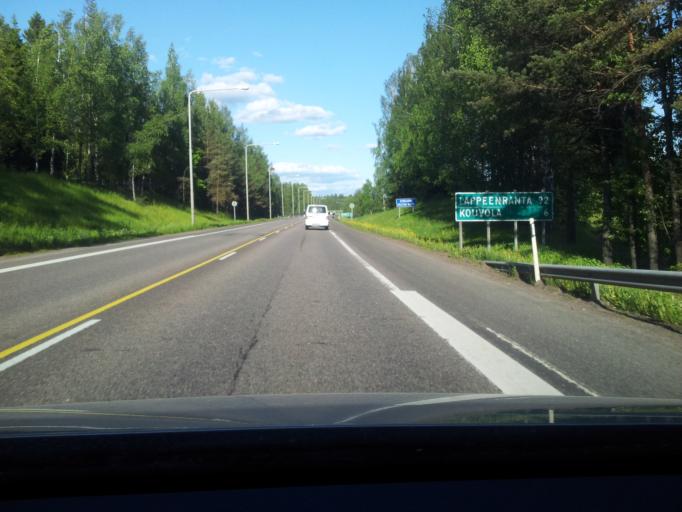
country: FI
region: Kymenlaakso
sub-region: Kouvola
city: Kouvola
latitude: 60.8733
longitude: 26.6088
